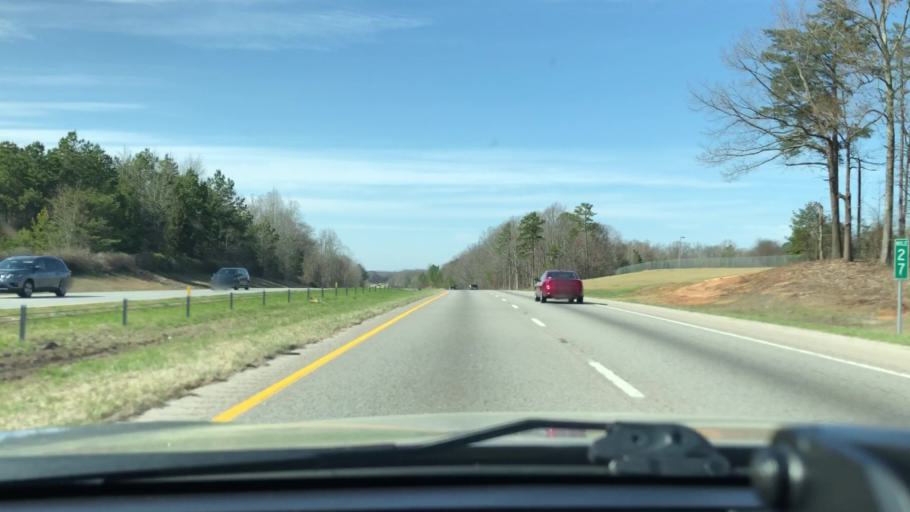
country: US
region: South Carolina
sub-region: Spartanburg County
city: Roebuck
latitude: 34.8538
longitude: -81.9772
